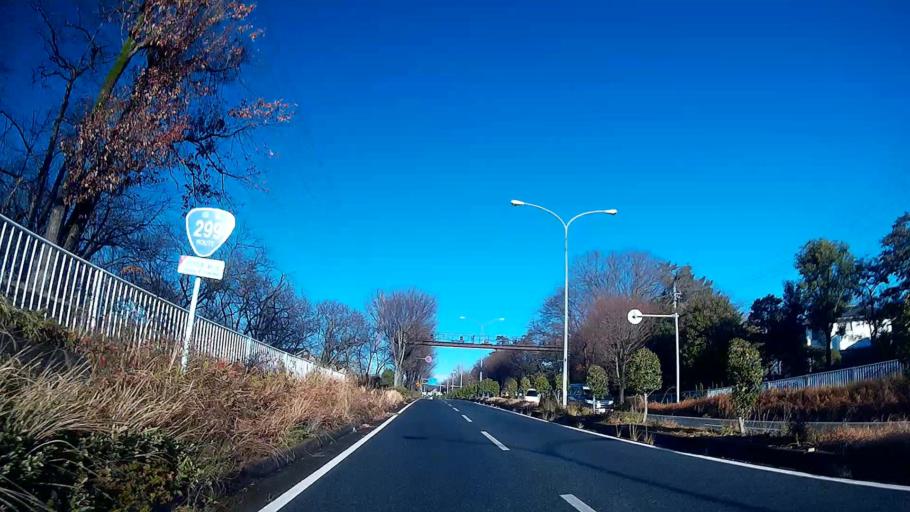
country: JP
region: Saitama
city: Hanno
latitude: 35.8546
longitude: 139.3588
